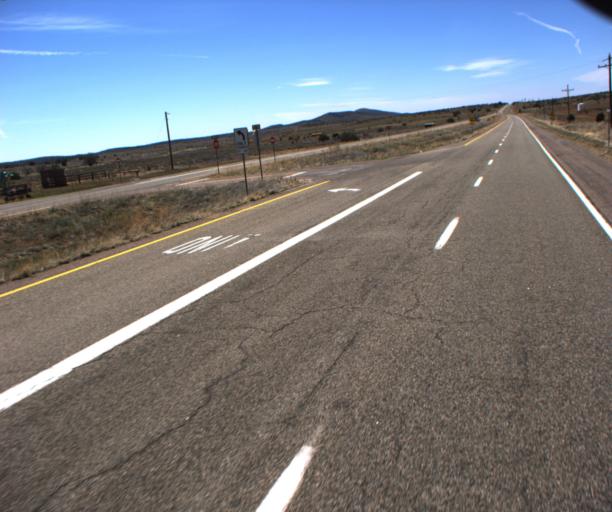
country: US
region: Arizona
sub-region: Mohave County
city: Peach Springs
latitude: 35.5304
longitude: -113.2315
